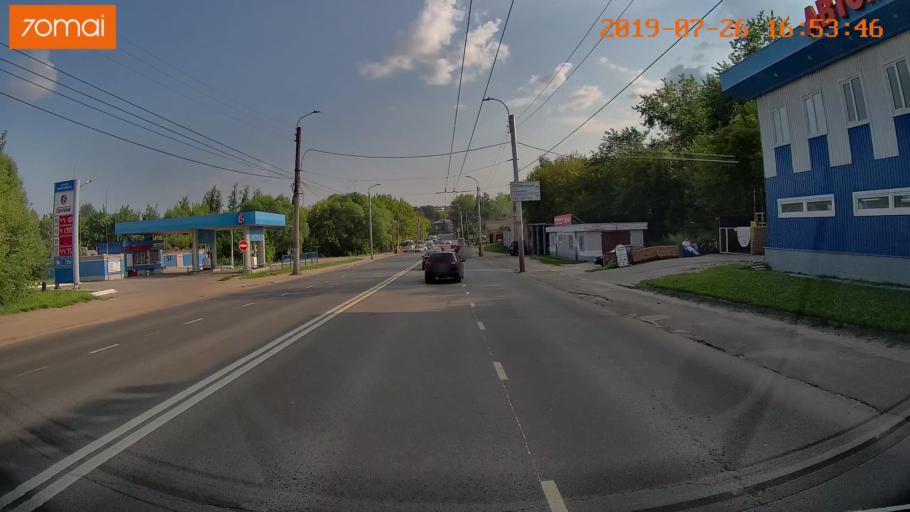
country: RU
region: Ivanovo
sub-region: Gorod Ivanovo
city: Ivanovo
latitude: 57.0131
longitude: 41.0012
